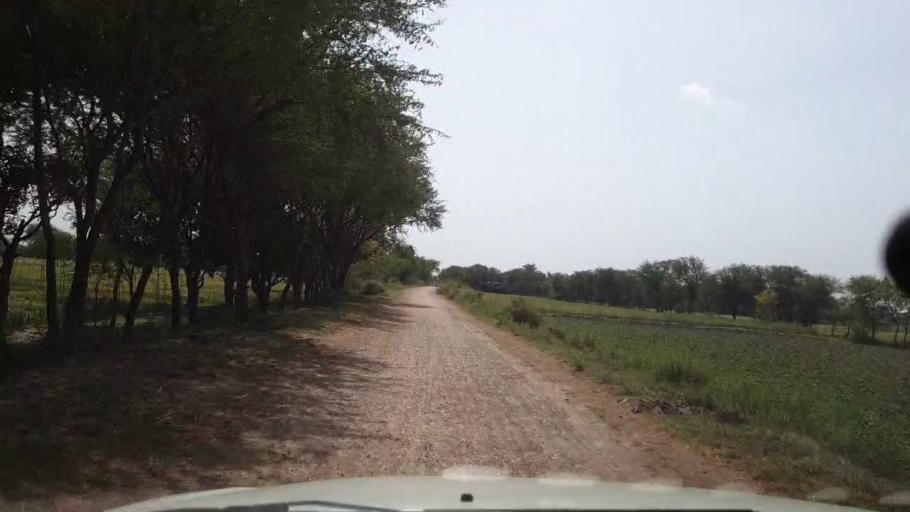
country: PK
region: Sindh
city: Matli
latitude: 25.0217
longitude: 68.7116
